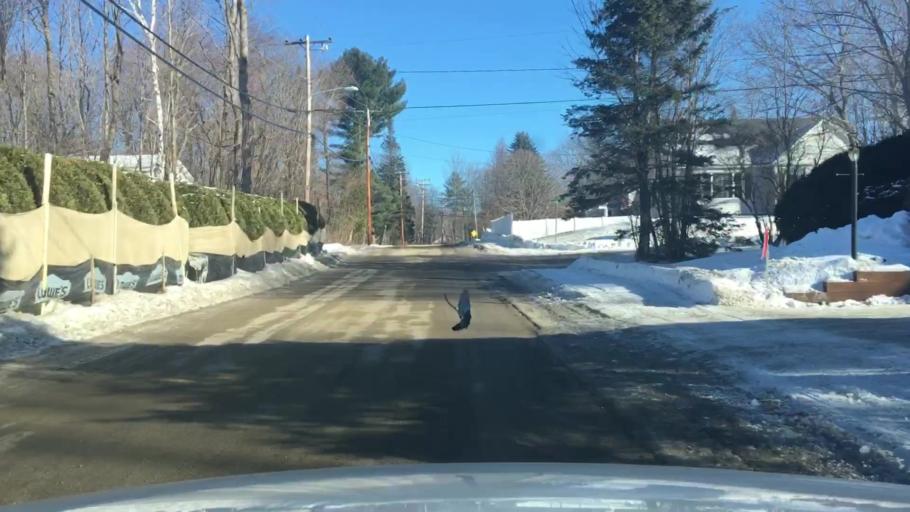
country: US
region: Maine
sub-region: Kennebec County
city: Winthrop
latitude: 44.3112
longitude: -69.9699
